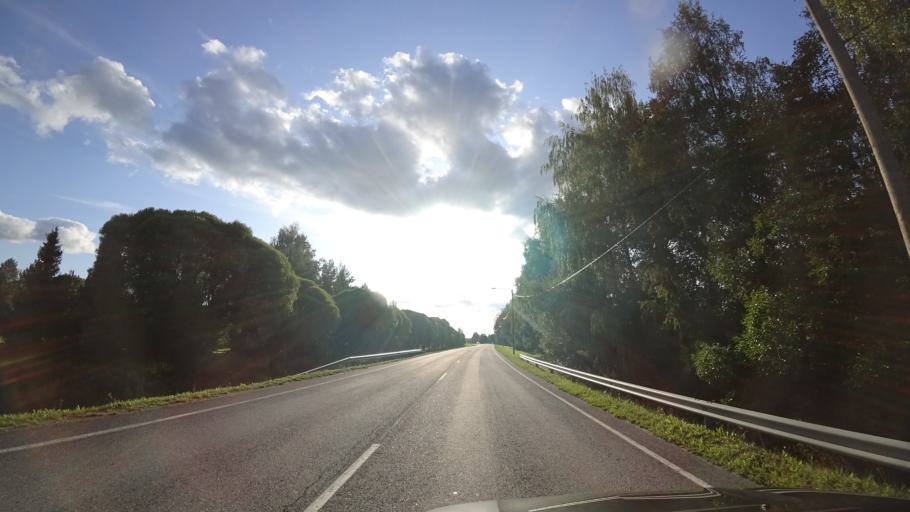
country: FI
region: Haeme
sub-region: Haemeenlinna
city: Lammi
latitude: 61.0776
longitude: 25.0187
